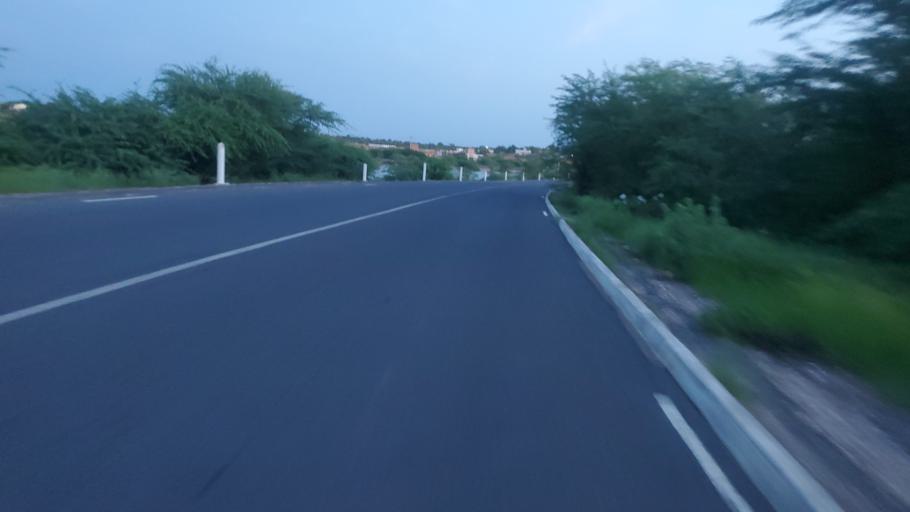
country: SN
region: Saint-Louis
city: Saint-Louis
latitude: 16.0745
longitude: -16.3892
